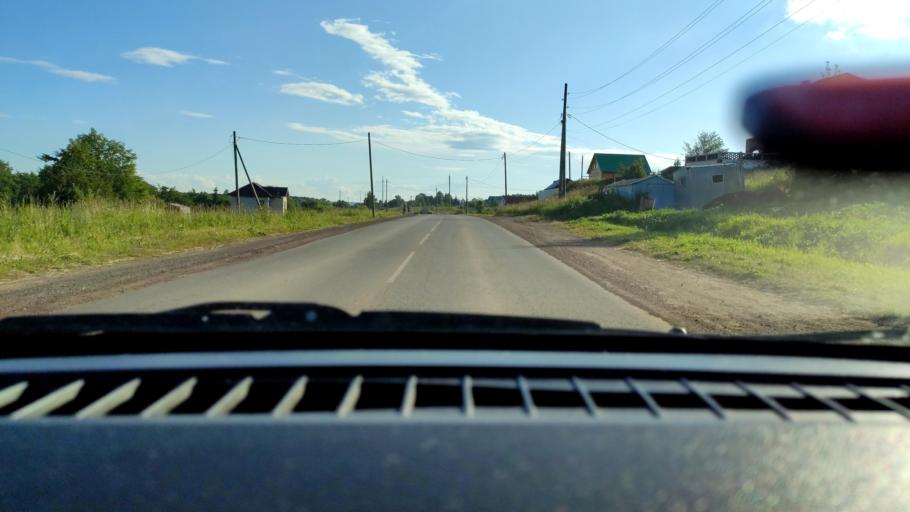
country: RU
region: Perm
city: Kultayevo
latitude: 57.8980
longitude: 55.9203
